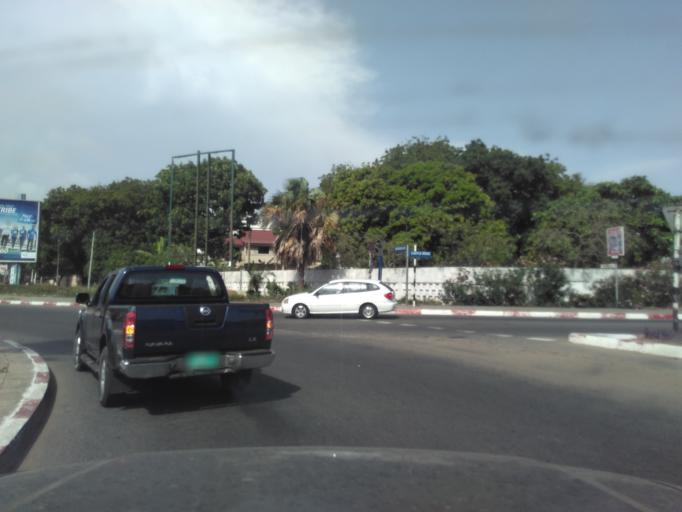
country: GH
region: Greater Accra
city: Accra
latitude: 5.5592
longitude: -0.1971
